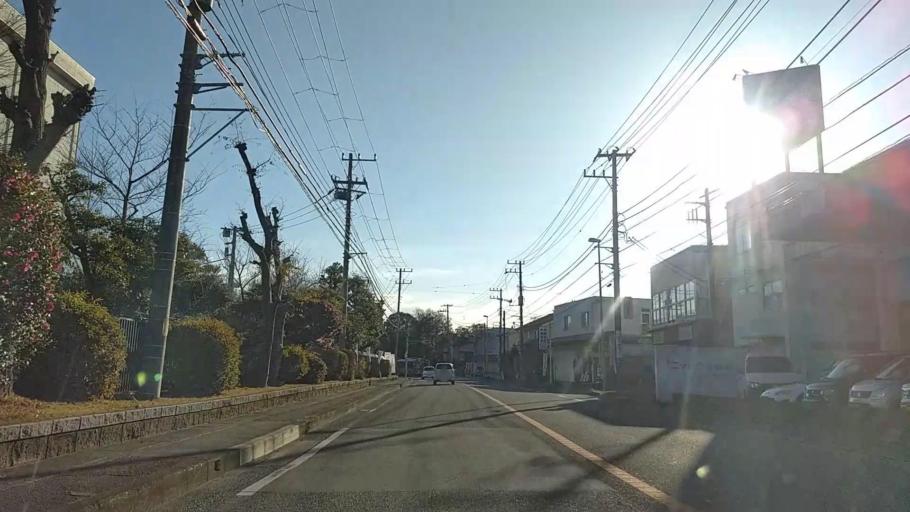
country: JP
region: Kanagawa
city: Fujisawa
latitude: 35.3469
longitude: 139.4623
